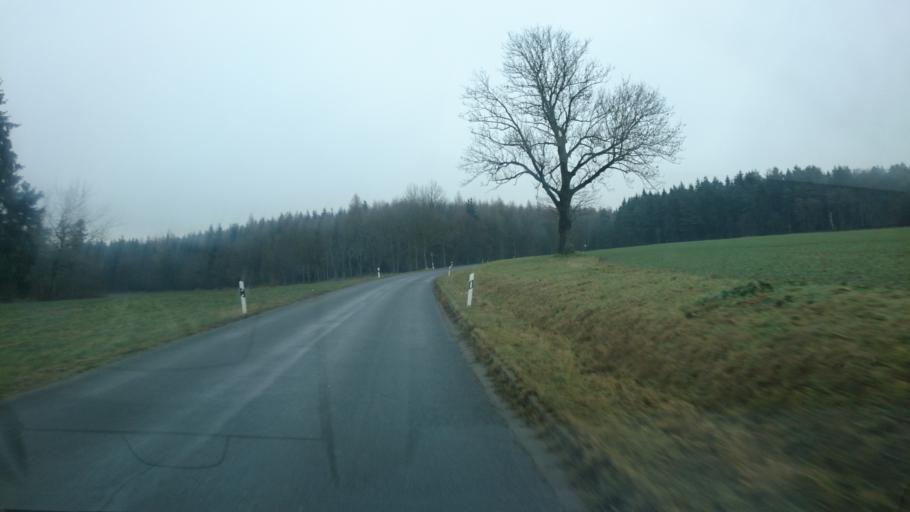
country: DE
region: Thuringia
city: Tanna
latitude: 50.5119
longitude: 11.8670
